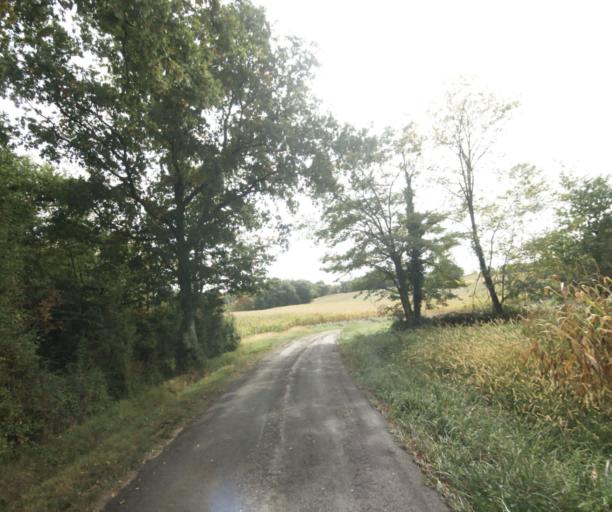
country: FR
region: Midi-Pyrenees
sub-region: Departement du Gers
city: Eauze
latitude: 43.8652
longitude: 0.0699
